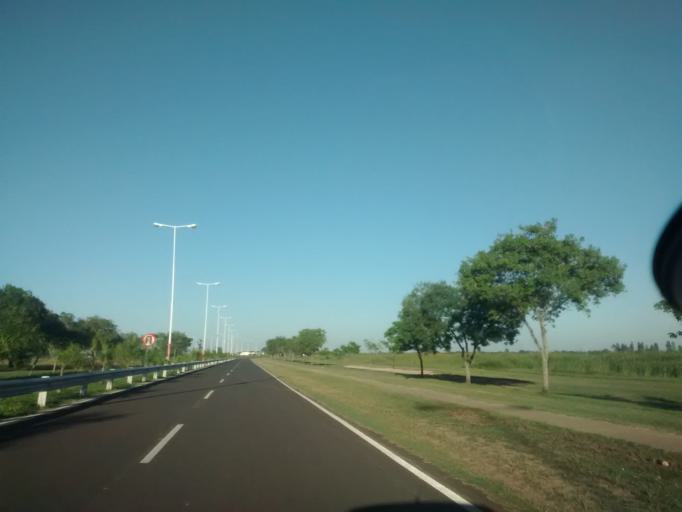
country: AR
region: Chaco
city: Fontana
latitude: -27.4417
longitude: -59.0364
